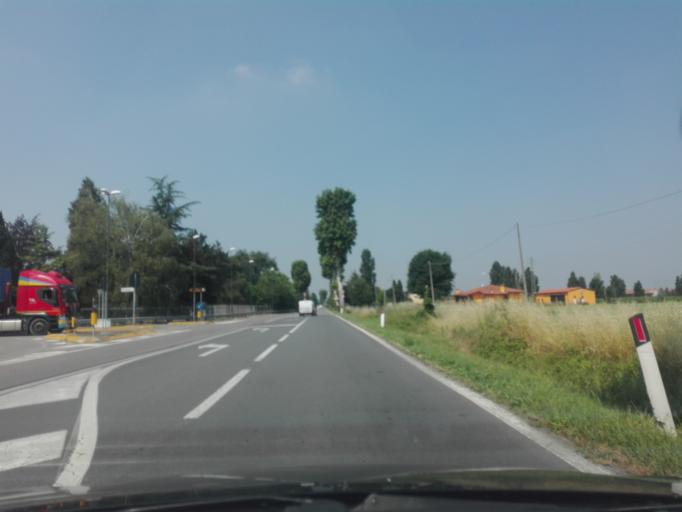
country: IT
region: Veneto
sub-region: Provincia di Rovigo
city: Lama Pezzoli
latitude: 45.0640
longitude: 11.9256
